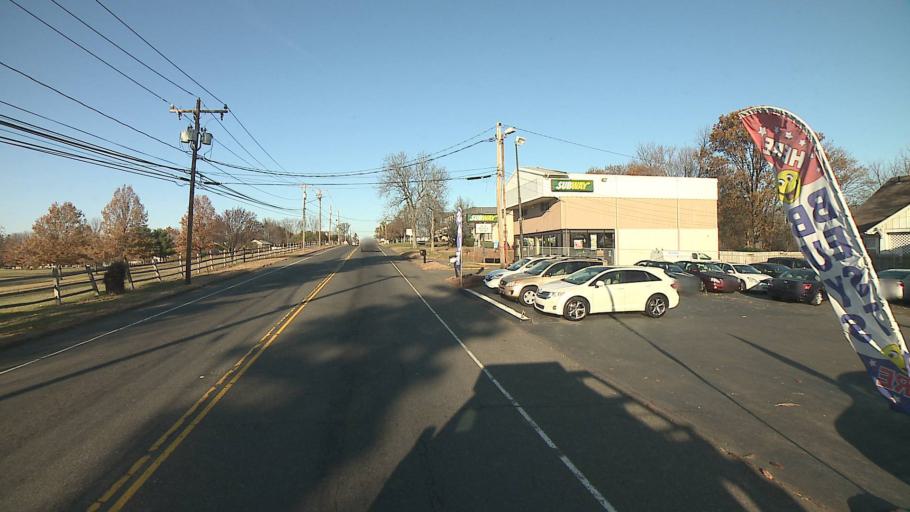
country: US
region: Connecticut
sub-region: New Haven County
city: Meriden
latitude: 41.5147
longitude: -72.8053
